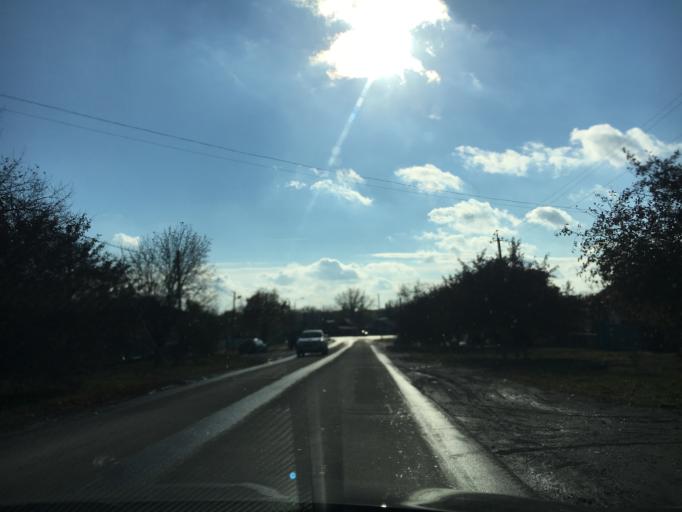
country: RU
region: Rostov
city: Matveyev Kurgan
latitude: 47.5680
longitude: 38.8710
